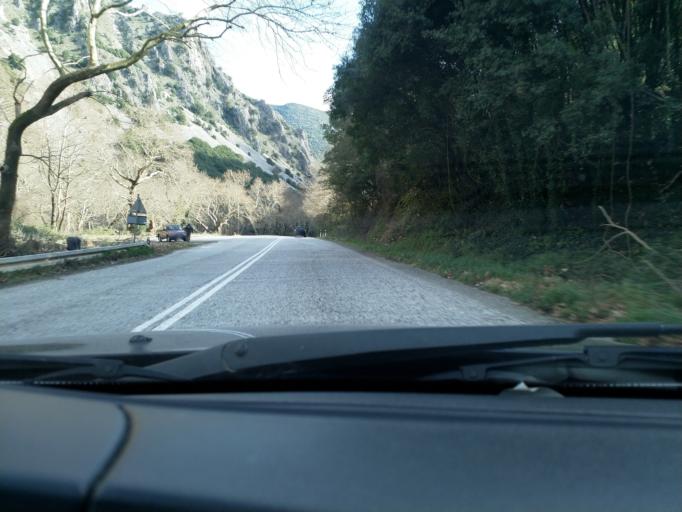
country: GR
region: Epirus
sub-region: Nomos Prevezis
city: Pappadates
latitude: 39.3970
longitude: 20.8387
